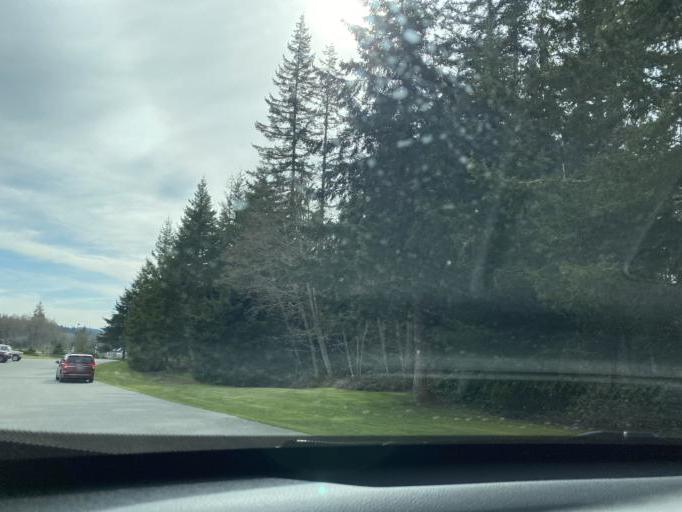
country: US
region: Washington
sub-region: Island County
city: Langley
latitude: 48.0080
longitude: -122.4086
